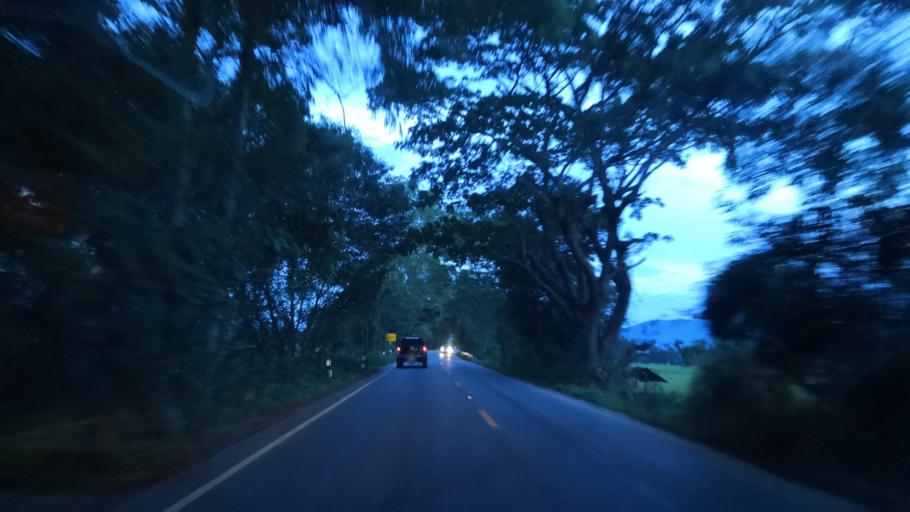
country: TH
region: Chiang Rai
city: Wiang Chai
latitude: 19.9709
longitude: 99.9688
